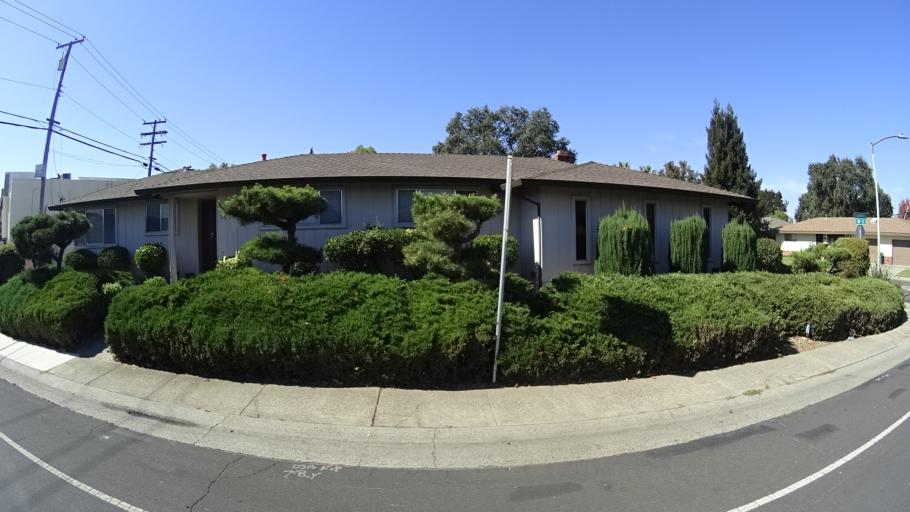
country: US
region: California
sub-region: Sacramento County
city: Parkway
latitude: 38.4980
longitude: -121.5103
